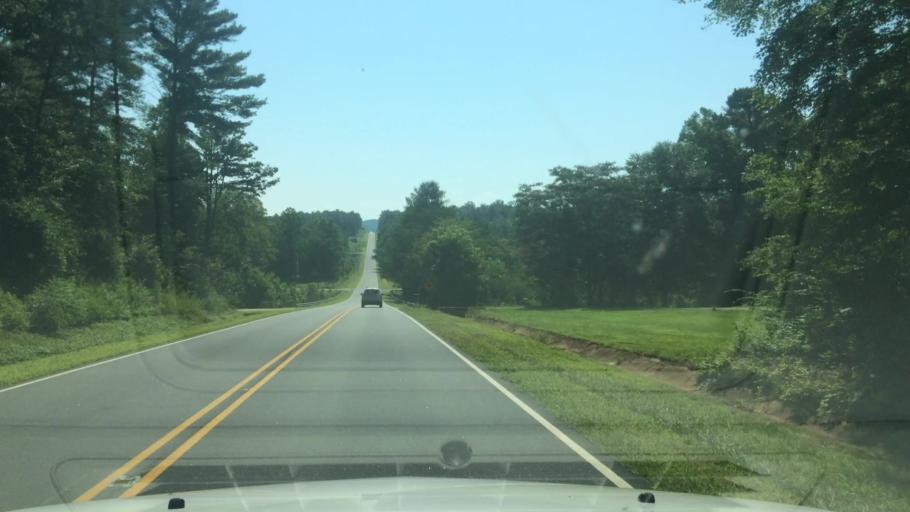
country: US
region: North Carolina
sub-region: Caldwell County
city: Hudson
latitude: 35.9086
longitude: -81.4174
